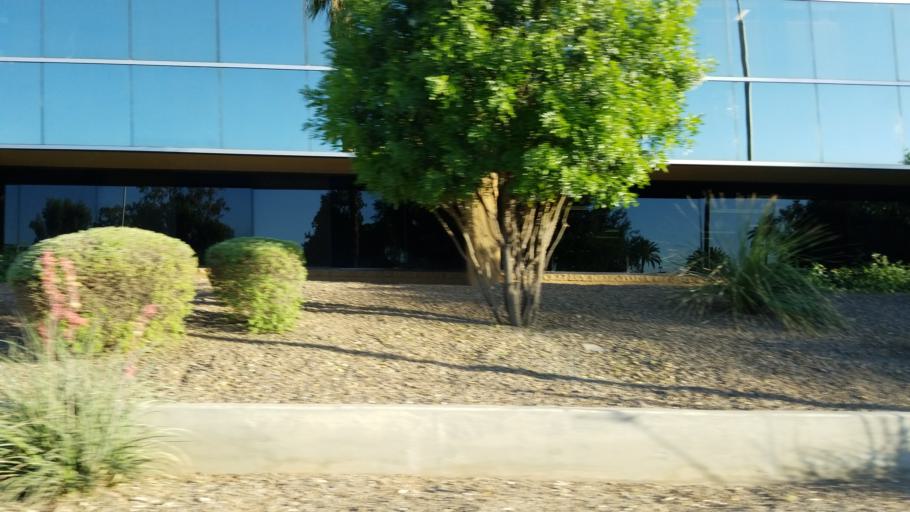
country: US
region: Arizona
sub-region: Maricopa County
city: Paradise Valley
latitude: 33.5097
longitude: -112.0179
